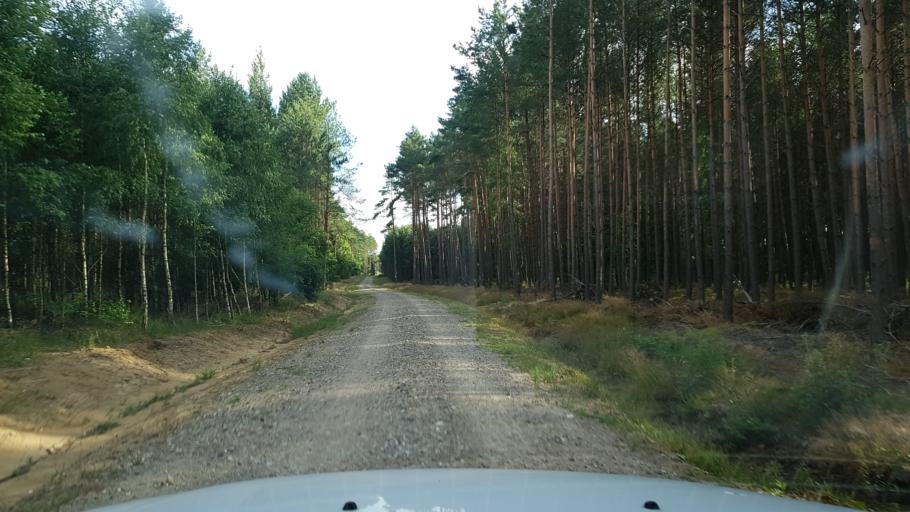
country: PL
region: West Pomeranian Voivodeship
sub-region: Powiat kolobrzeski
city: Grzybowo
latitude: 54.1019
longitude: 15.5389
